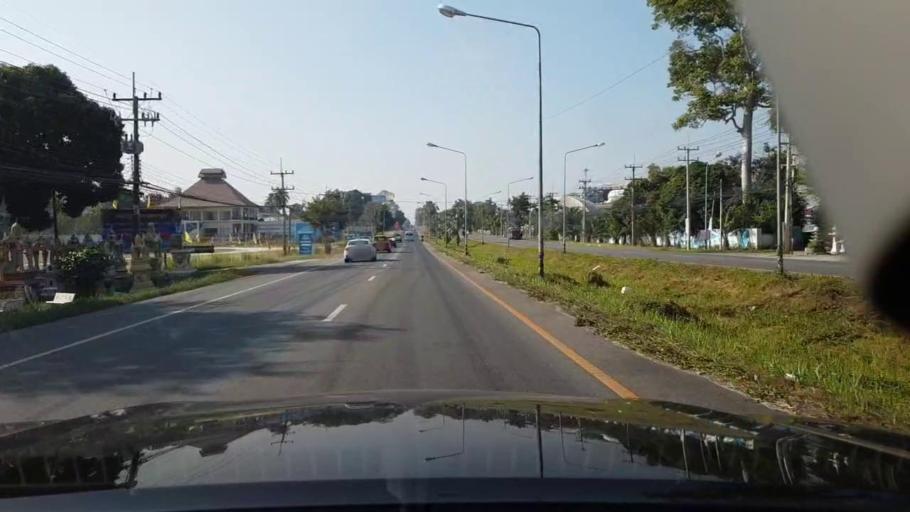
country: TH
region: Chon Buri
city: Sattahip
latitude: 12.7873
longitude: 100.9164
